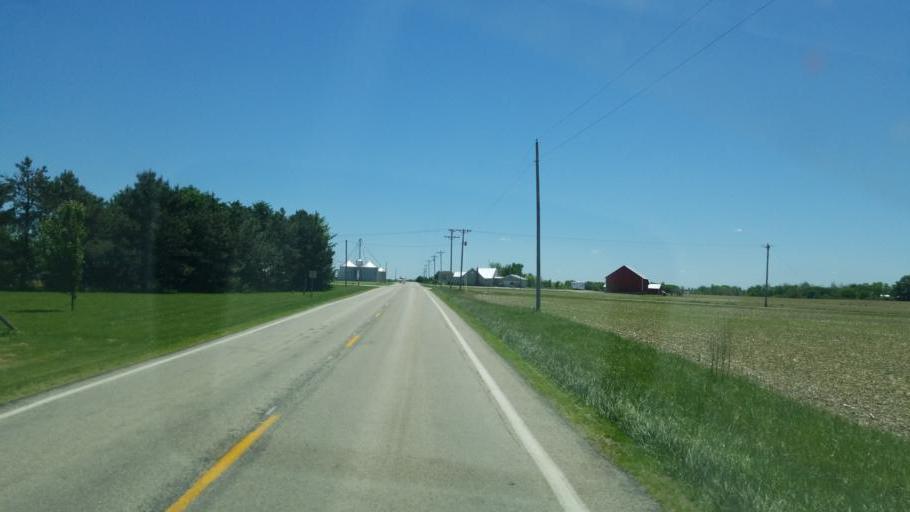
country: US
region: Ohio
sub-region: Darke County
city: Ansonia
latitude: 40.2660
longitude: -84.7010
